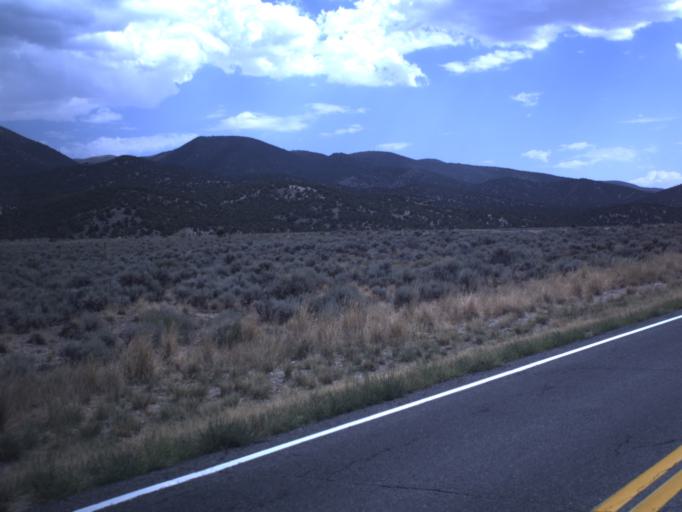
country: US
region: Utah
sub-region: Tooele County
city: Tooele
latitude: 40.3523
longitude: -112.3115
